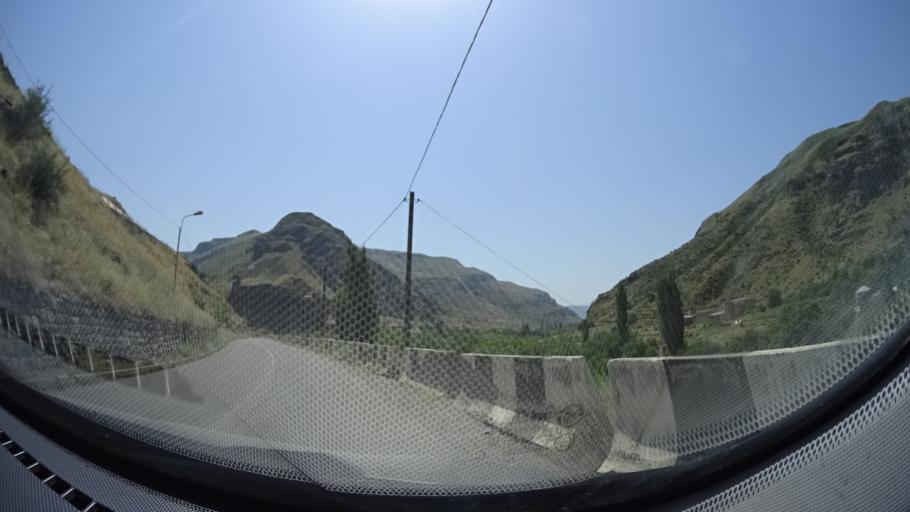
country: GE
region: Samtskhe-Javakheti
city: Aspindza
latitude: 41.4810
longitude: 43.2812
